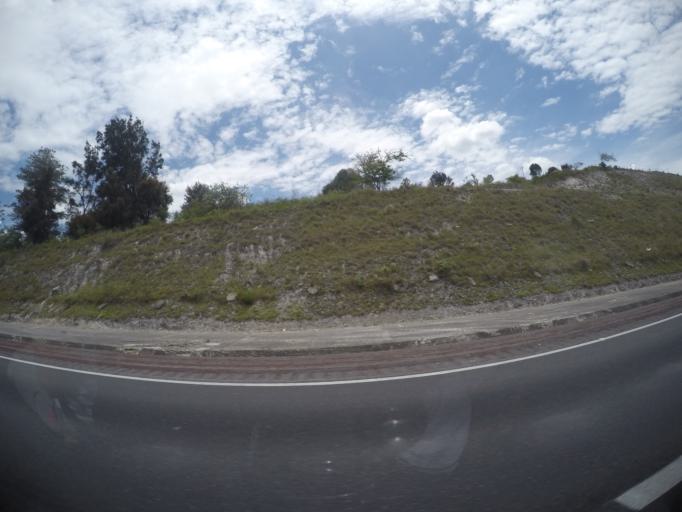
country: MX
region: Guerrero
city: Petaquillas
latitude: 17.4826
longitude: -99.4742
